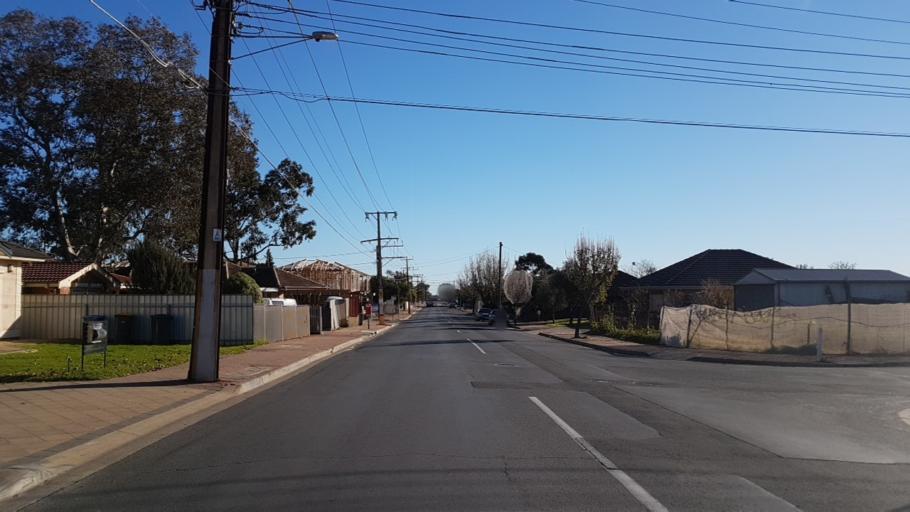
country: AU
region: South Australia
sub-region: Campbelltown
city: Paradise
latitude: -34.8813
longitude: 138.6817
